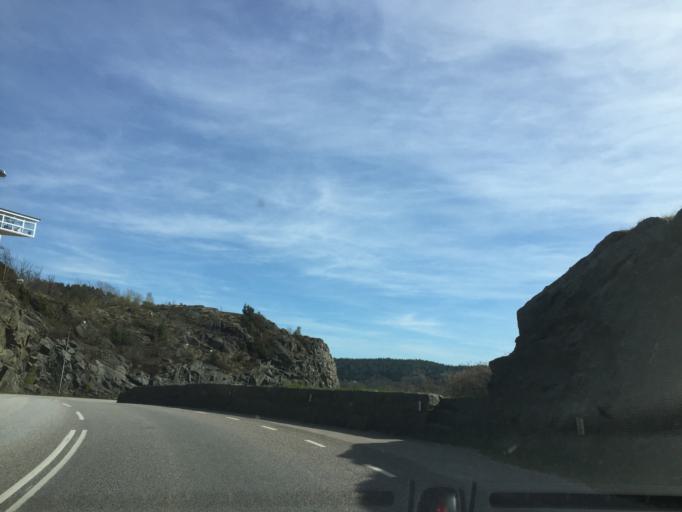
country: SE
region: Vaestra Goetaland
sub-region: Uddevalla Kommun
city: Uddevalla
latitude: 58.3375
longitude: 11.9074
